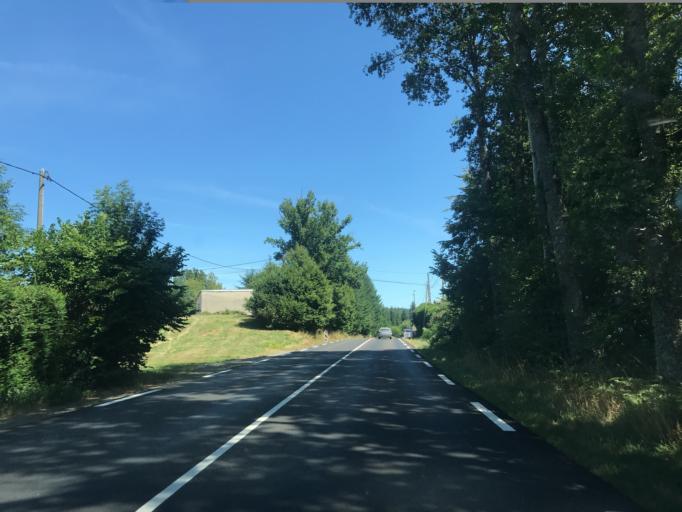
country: FR
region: Limousin
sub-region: Departement de la Correze
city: Egletons
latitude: 45.3835
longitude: 2.0178
